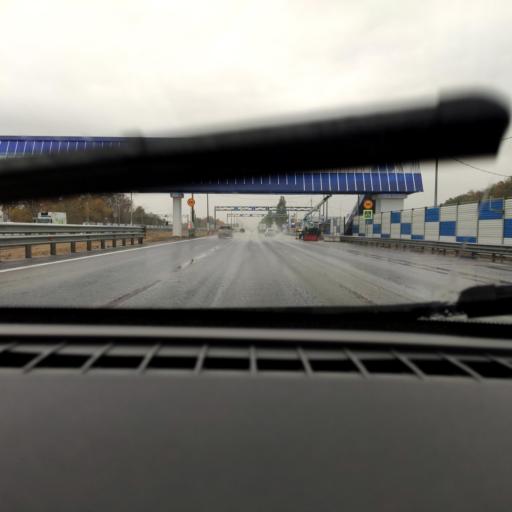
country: RU
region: Voronezj
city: Podgornoye
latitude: 51.7732
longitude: 39.1918
